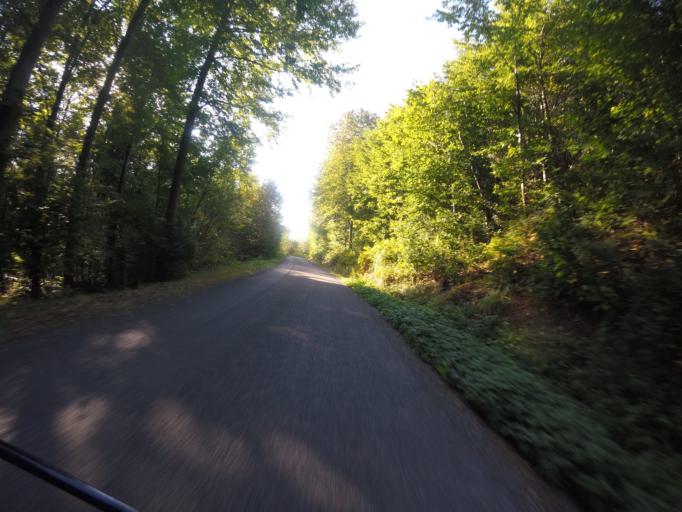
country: DE
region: Baden-Wuerttemberg
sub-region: Regierungsbezirk Stuttgart
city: Oppenweiler
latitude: 48.9878
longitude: 9.4280
